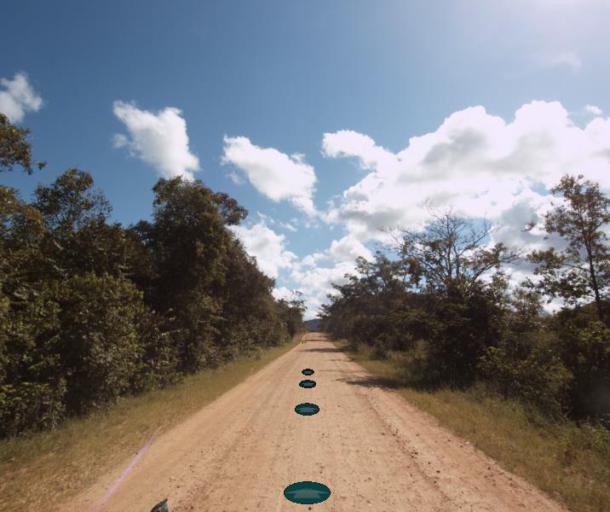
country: BR
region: Goias
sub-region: Pirenopolis
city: Pirenopolis
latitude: -15.7923
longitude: -49.0783
